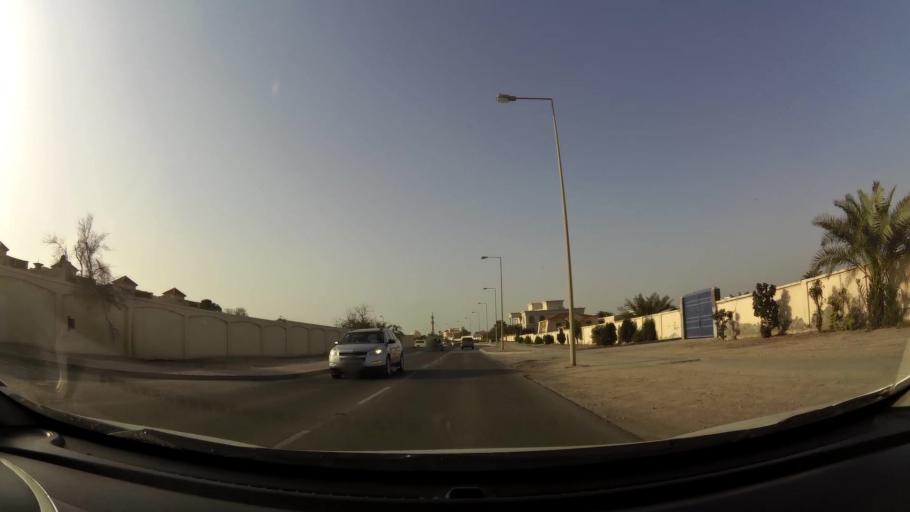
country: BH
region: Manama
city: Jidd Hafs
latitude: 26.2077
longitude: 50.4824
